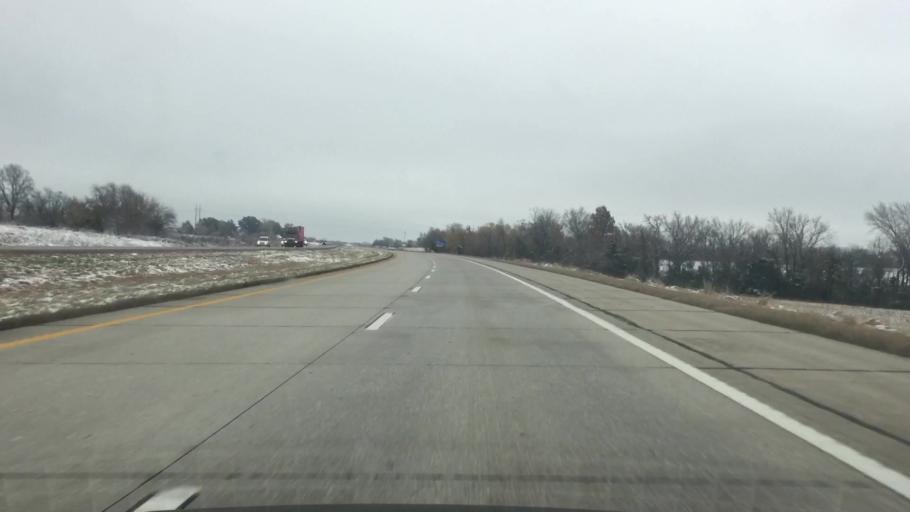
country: US
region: Missouri
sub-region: Saint Clair County
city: Osceola
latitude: 38.1889
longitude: -93.7389
